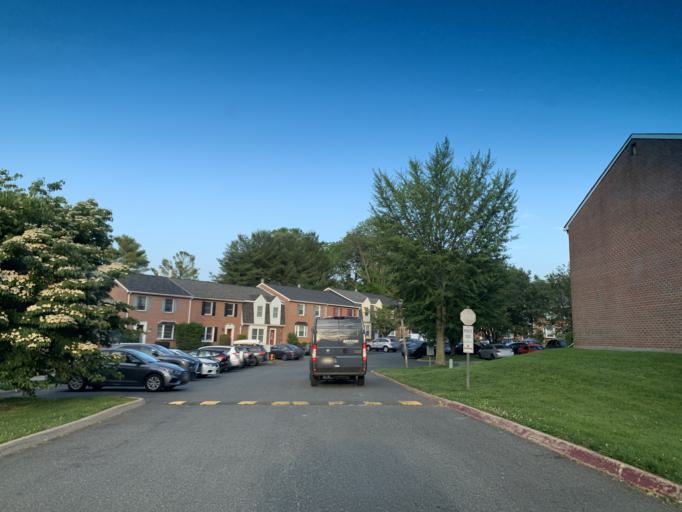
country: US
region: Maryland
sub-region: Harford County
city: North Bel Air
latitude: 39.5486
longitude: -76.3560
